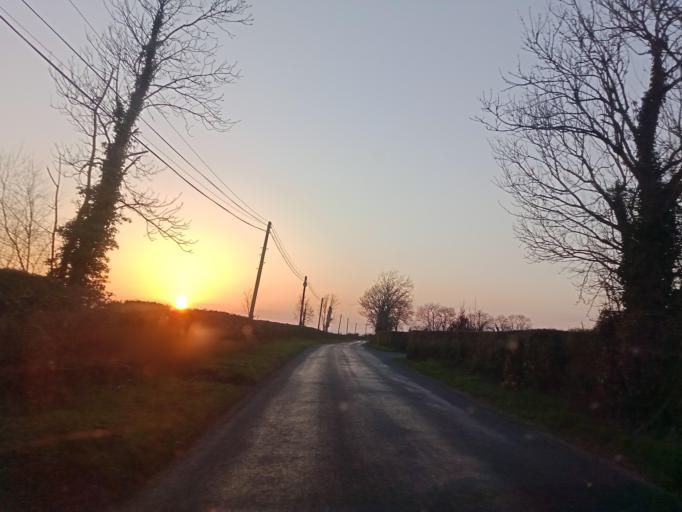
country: IE
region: Leinster
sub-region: Laois
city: Abbeyleix
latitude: 52.9492
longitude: -7.3490
